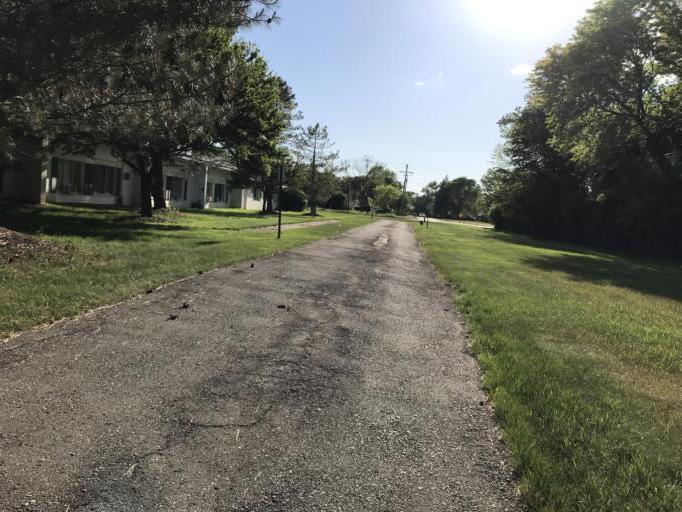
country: US
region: Michigan
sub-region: Oakland County
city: Farmington
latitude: 42.4733
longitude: -83.3365
